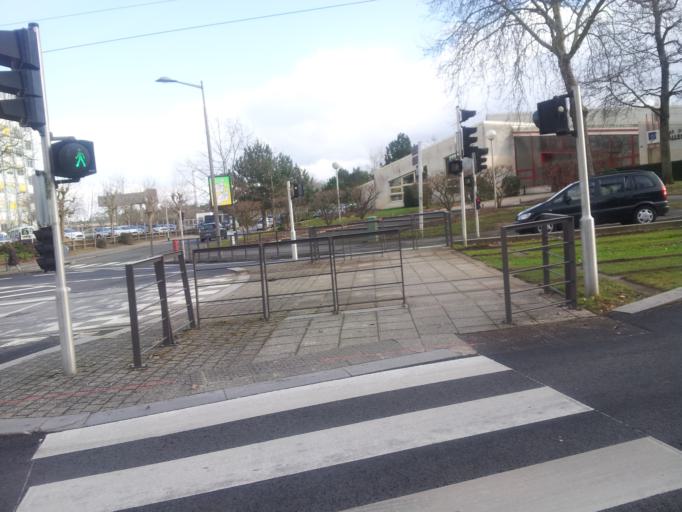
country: FR
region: Centre
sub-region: Departement du Loiret
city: Saint-Cyr-en-Val
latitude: 47.8349
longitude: 1.9312
